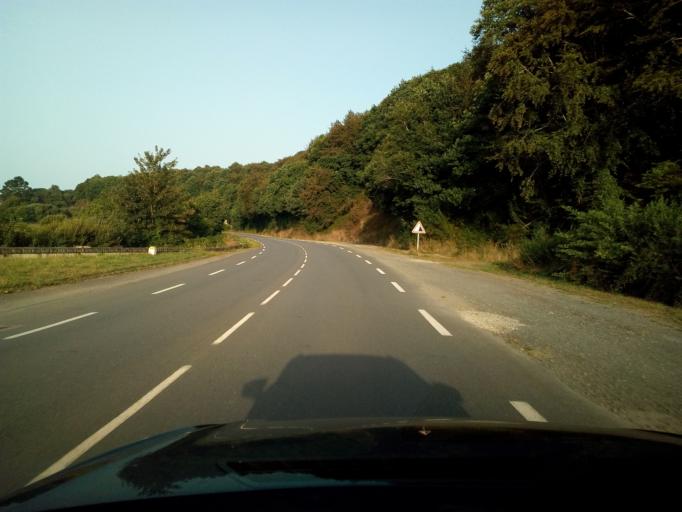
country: FR
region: Brittany
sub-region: Departement du Finistere
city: La Roche-Maurice
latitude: 48.4699
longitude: -4.2202
